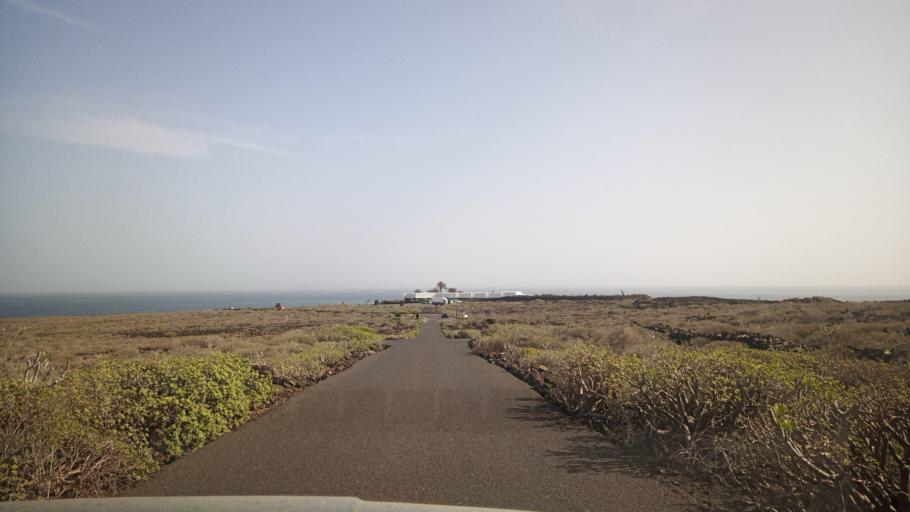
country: ES
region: Canary Islands
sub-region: Provincia de Las Palmas
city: Haria
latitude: 29.1590
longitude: -13.4357
